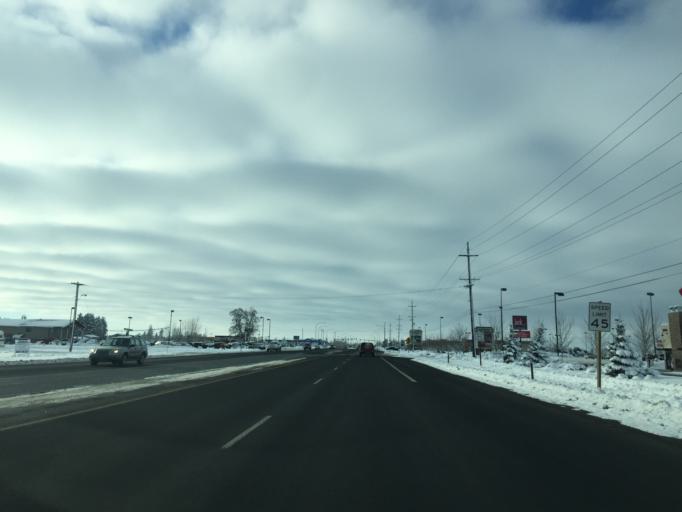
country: US
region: Washington
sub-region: Spokane County
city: Airway Heights
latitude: 47.6431
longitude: -117.5549
